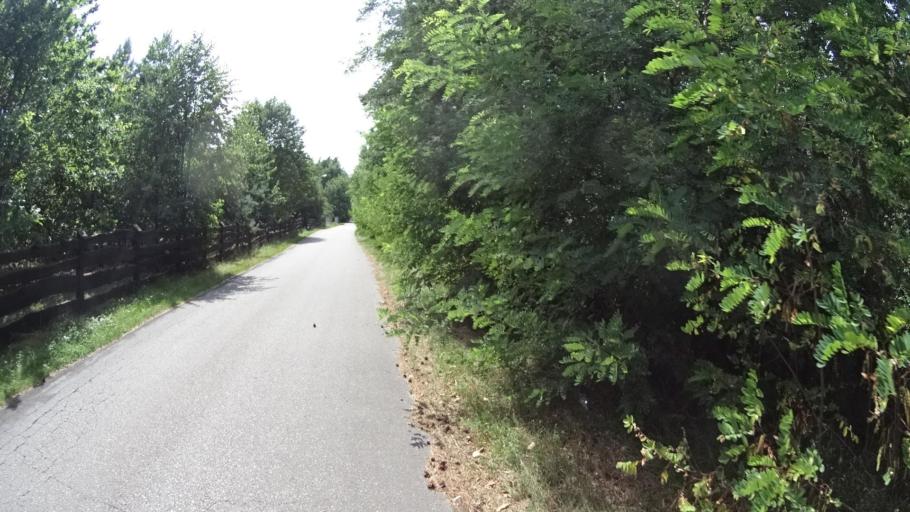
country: PL
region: Masovian Voivodeship
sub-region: Powiat bialobrzeski
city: Wysmierzyce
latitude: 51.6383
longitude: 20.8693
